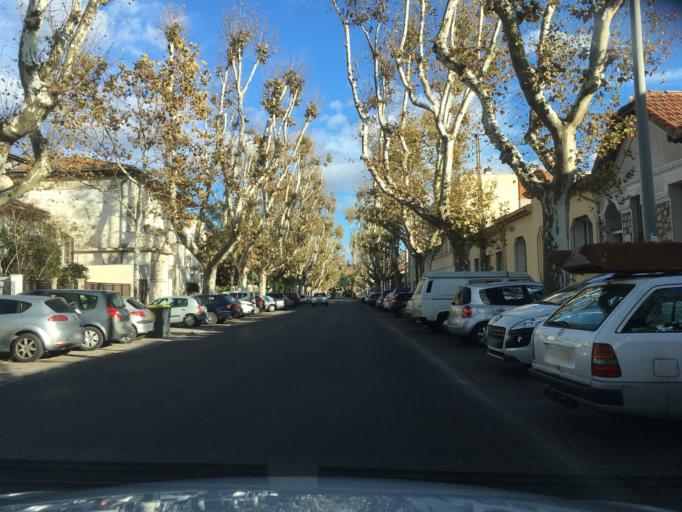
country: FR
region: Languedoc-Roussillon
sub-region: Departement de l'Herault
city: Montpellier
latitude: 43.6012
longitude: 3.8645
